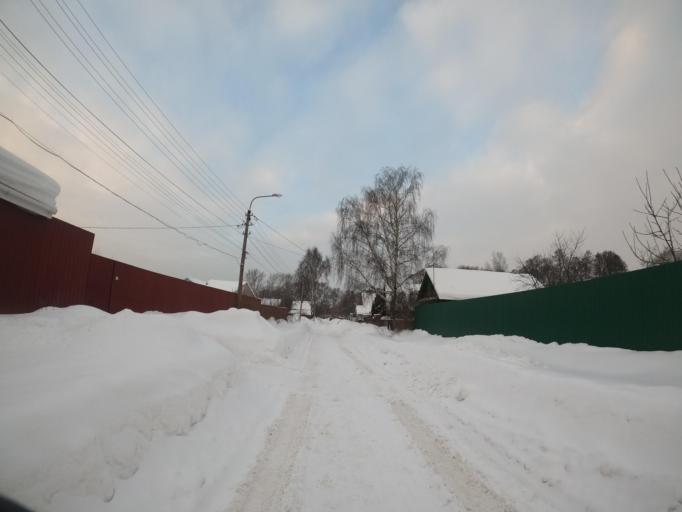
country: RU
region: Moskovskaya
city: Pavlovskiy Posad
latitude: 55.7719
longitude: 38.6307
